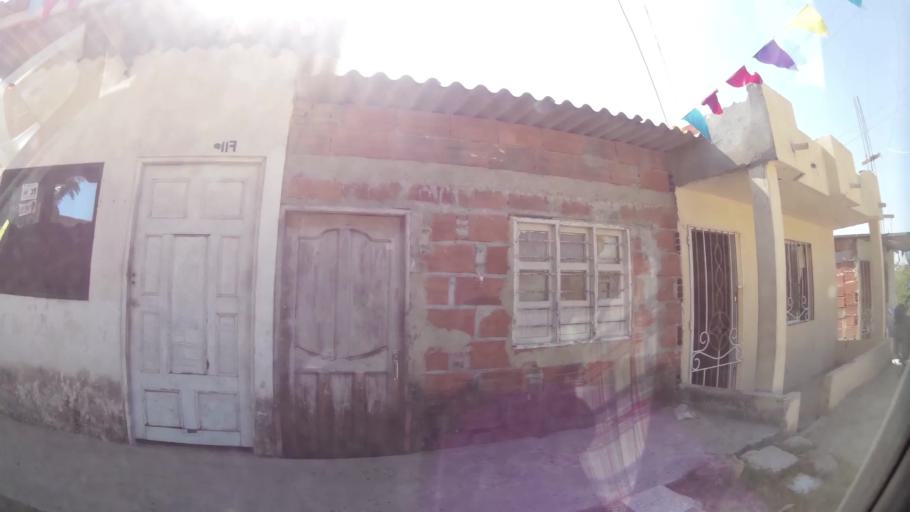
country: CO
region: Atlantico
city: Barranquilla
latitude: 10.9791
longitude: -74.8279
